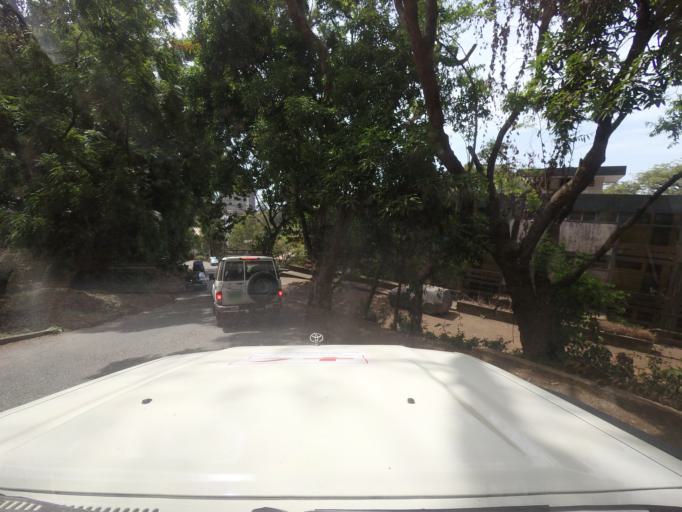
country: SL
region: Western Area
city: Freetown
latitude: 8.4765
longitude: -13.2200
